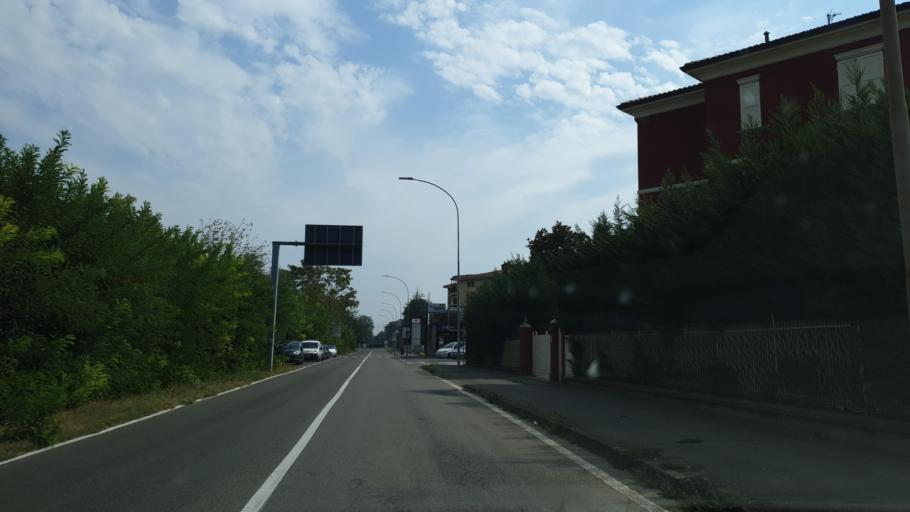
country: IT
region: Emilia-Romagna
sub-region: Provincia di Parma
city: Parma
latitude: 44.8141
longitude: 10.2908
